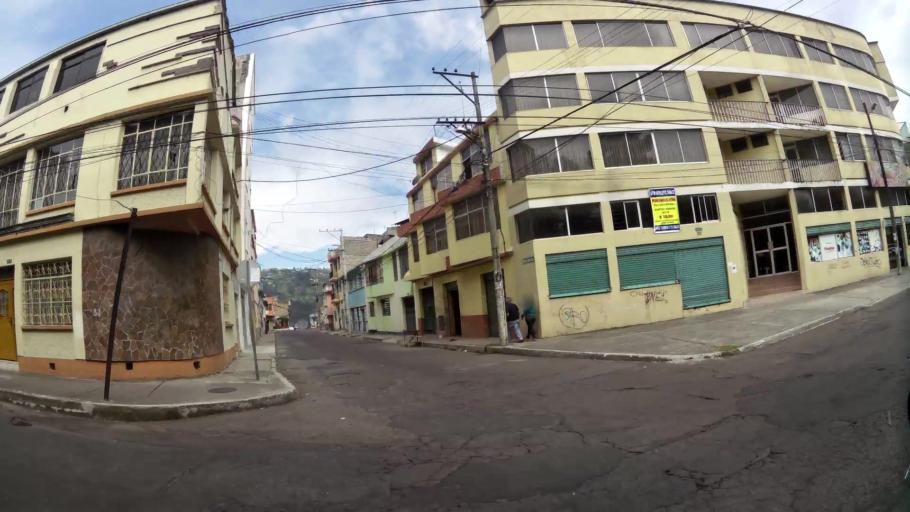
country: EC
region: Pichincha
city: Quito
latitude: -0.2147
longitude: -78.4877
